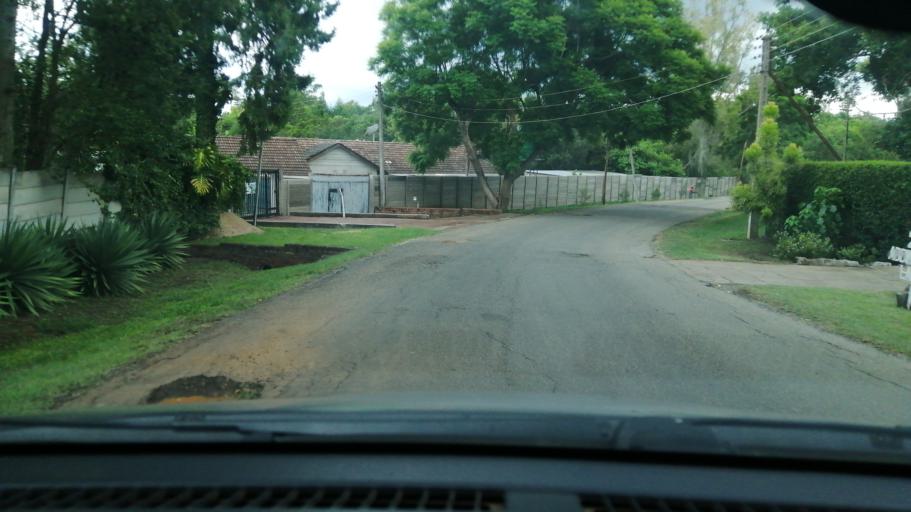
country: ZW
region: Harare
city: Harare
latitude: -17.7721
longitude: 31.0978
